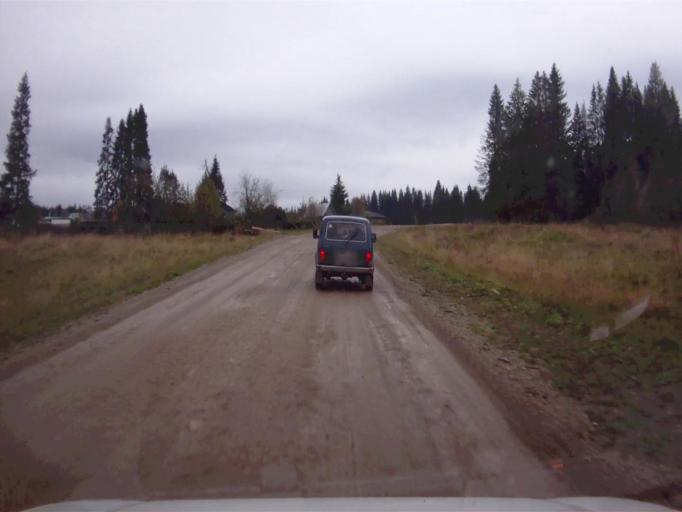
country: RU
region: Chelyabinsk
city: Nyazepetrovsk
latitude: 56.0622
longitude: 59.5649
